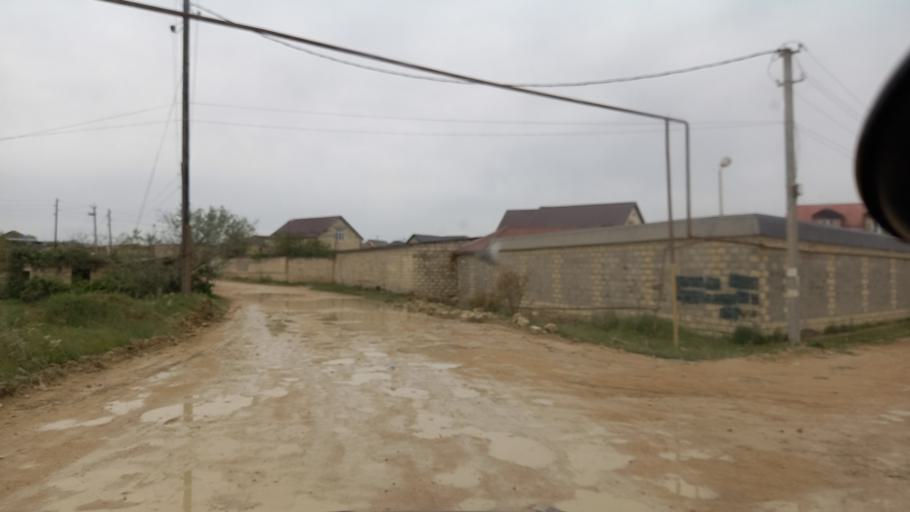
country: RU
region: Dagestan
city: Sabnova
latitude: 42.1202
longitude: 48.2648
